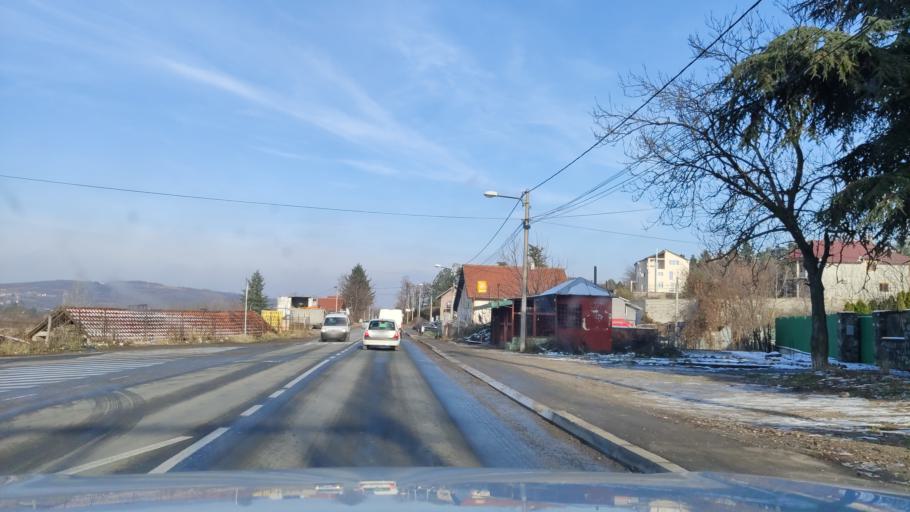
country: RS
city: Rusanj
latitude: 44.7019
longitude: 20.5050
